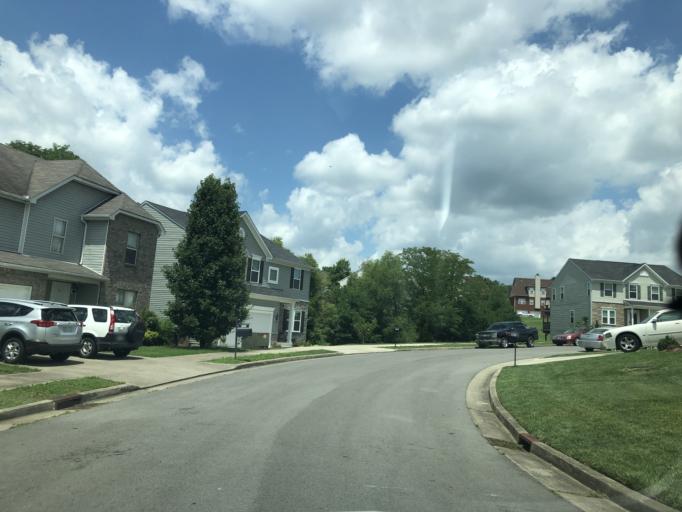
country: US
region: Tennessee
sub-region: Rutherford County
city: La Vergne
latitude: 36.0438
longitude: -86.6201
